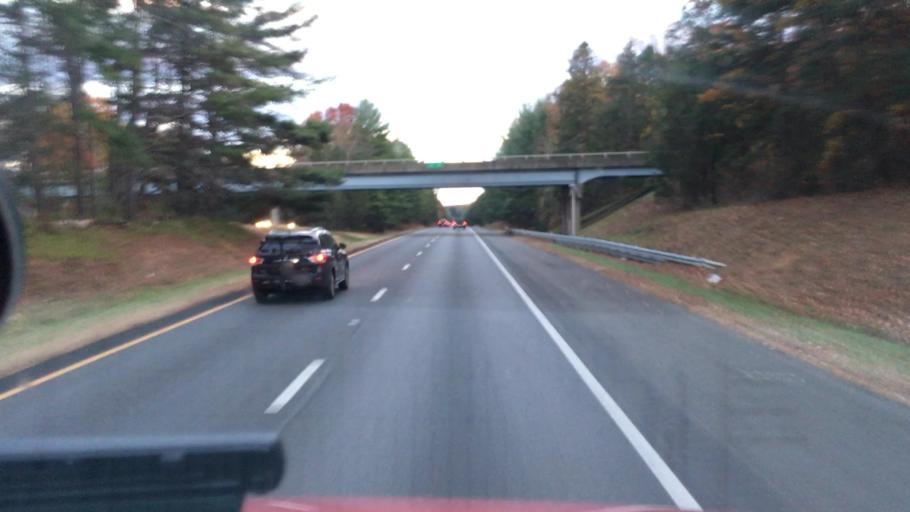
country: US
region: Virginia
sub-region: Fluvanna County
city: Palmyra
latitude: 37.9689
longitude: -78.1947
